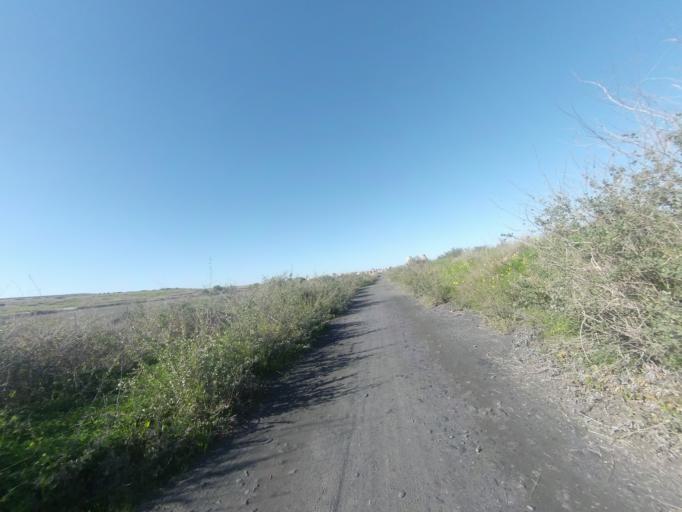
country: ES
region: Andalusia
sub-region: Provincia de Huelva
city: Palos de la Frontera
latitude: 37.2547
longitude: -6.9096
